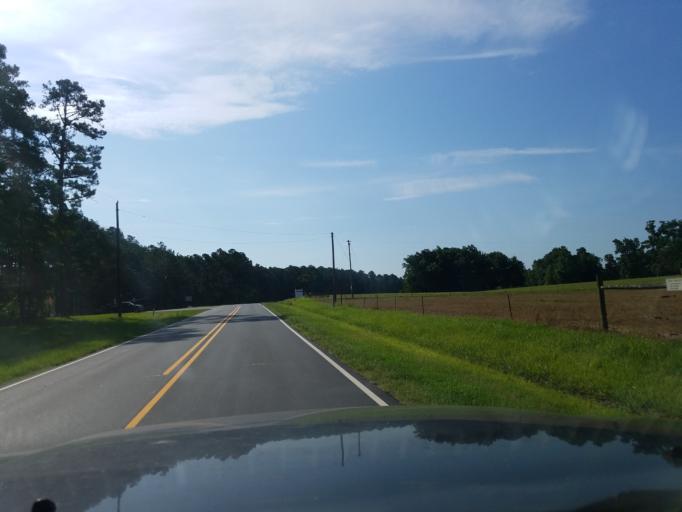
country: US
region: North Carolina
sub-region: Granville County
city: Butner
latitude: 36.1769
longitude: -78.7982
